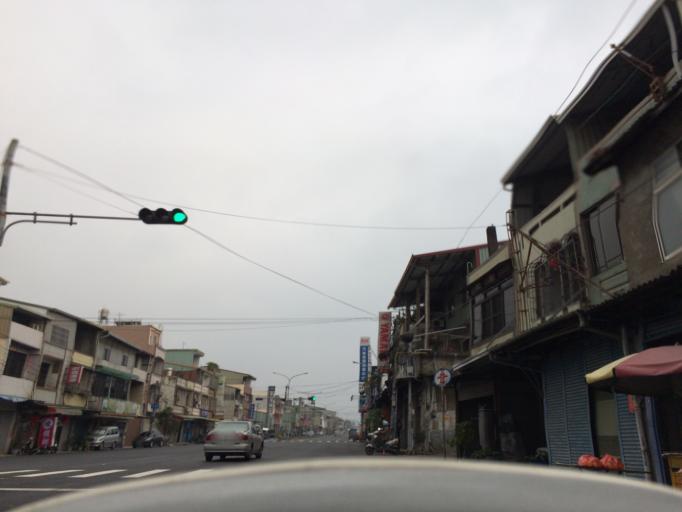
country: TW
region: Taiwan
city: Zhongxing New Village
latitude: 24.0269
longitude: 120.6968
